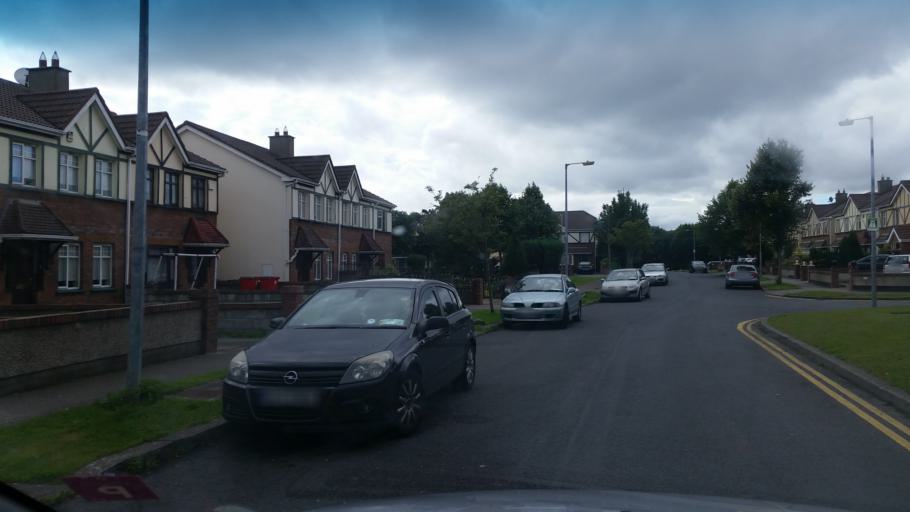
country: IE
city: Darndale
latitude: 53.3979
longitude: -6.1781
